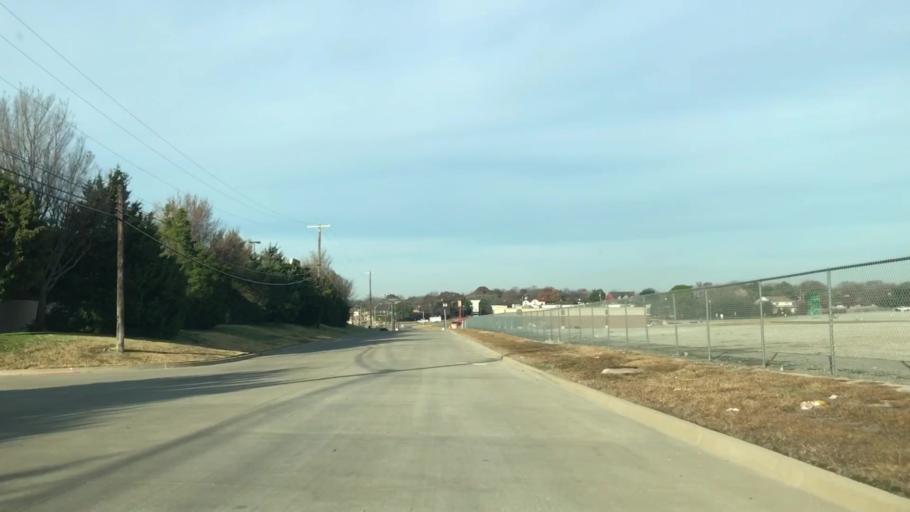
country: US
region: Texas
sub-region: Tarrant County
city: Sansom Park
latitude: 32.8167
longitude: -97.4158
